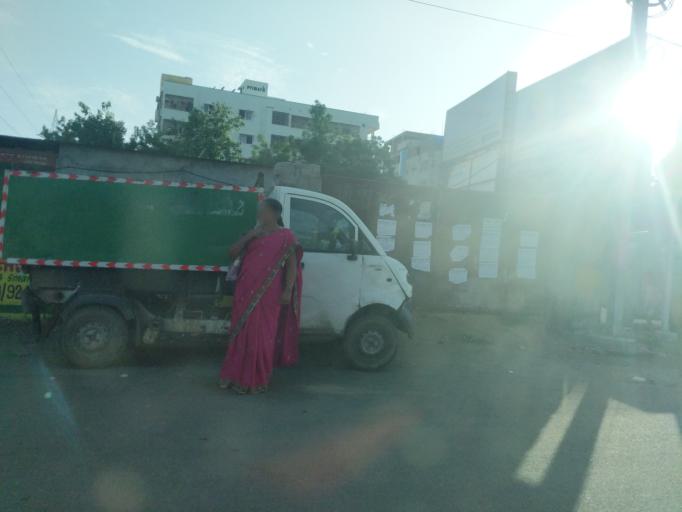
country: IN
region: Telangana
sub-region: Rangareddi
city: Kukatpalli
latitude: 17.4707
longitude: 78.3651
